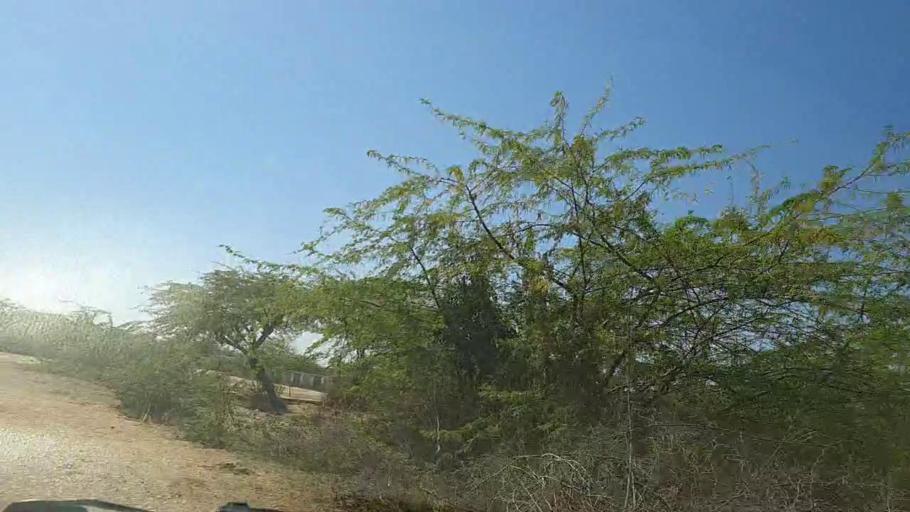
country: PK
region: Sindh
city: Dhoro Naro
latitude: 25.5162
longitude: 69.5251
